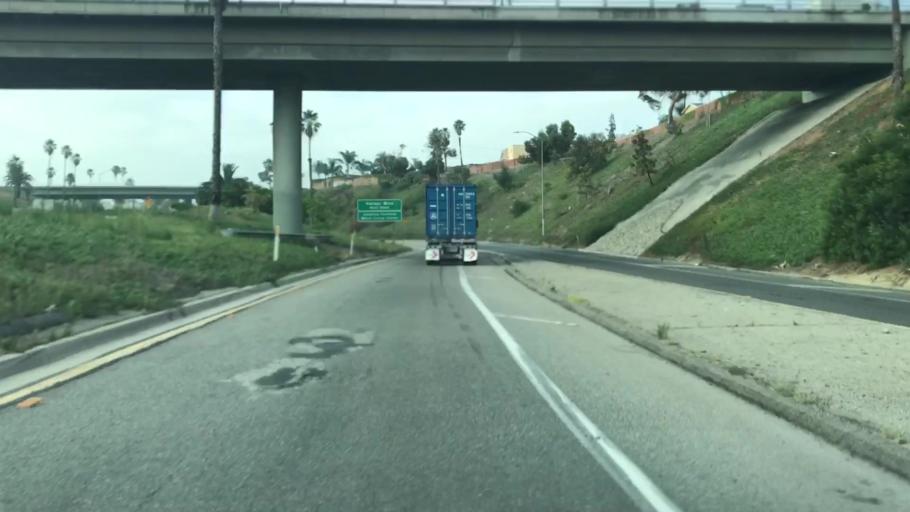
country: US
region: California
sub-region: Los Angeles County
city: San Pedro
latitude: 33.7525
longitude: -118.2915
